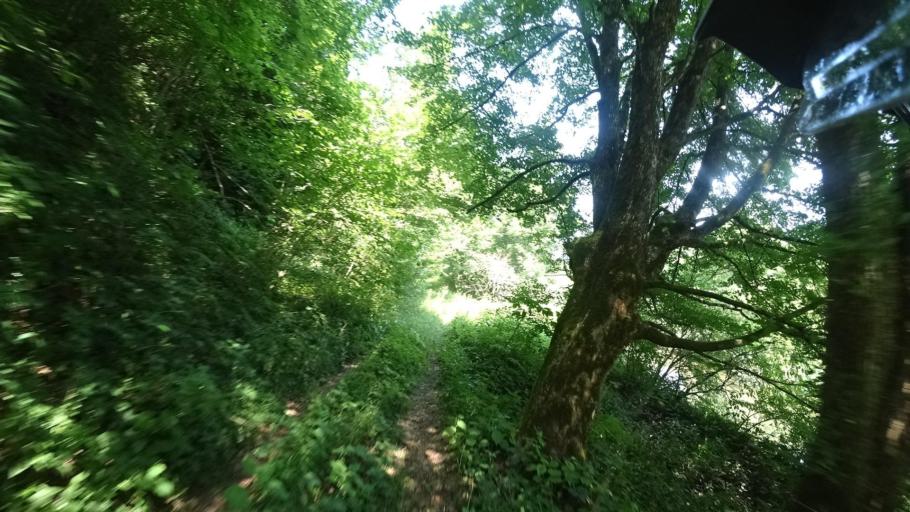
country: HR
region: Karlovacka
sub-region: Grad Ogulin
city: Ogulin
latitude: 45.3086
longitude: 15.1764
